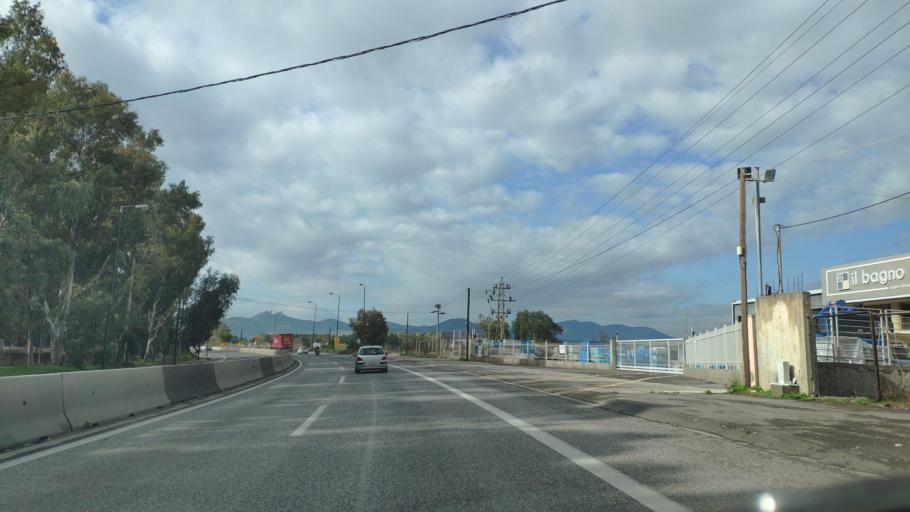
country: GR
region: Attica
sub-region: Nomarchia Dytikis Attikis
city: Elefsina
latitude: 38.0502
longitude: 23.5609
